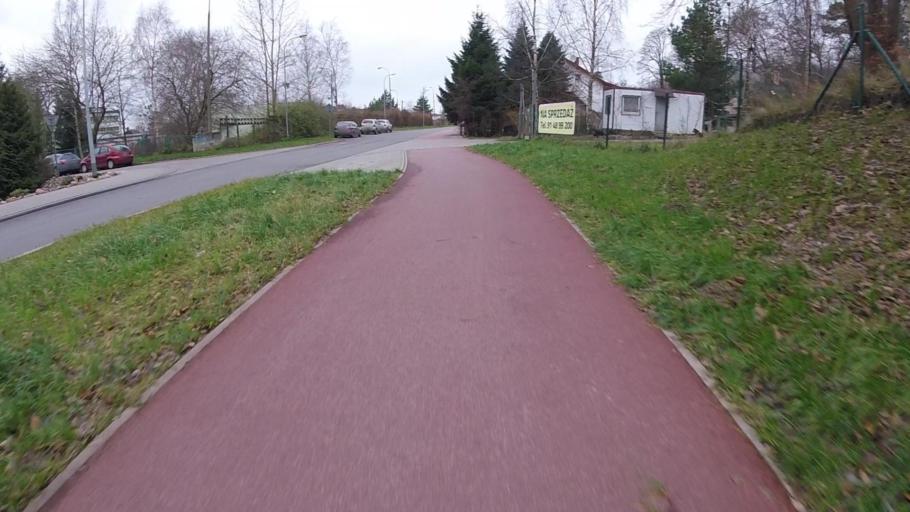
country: PL
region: West Pomeranian Voivodeship
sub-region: Koszalin
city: Koszalin
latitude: 54.1948
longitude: 16.2218
